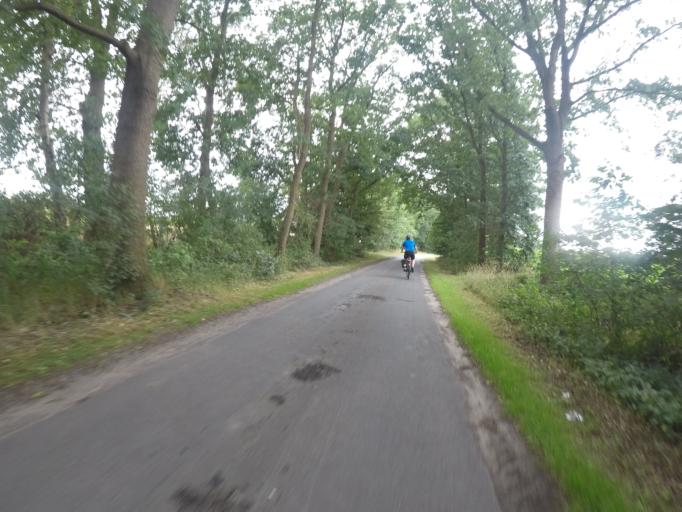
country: DE
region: Lower Saxony
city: Wingst
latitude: 53.6985
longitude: 9.0842
